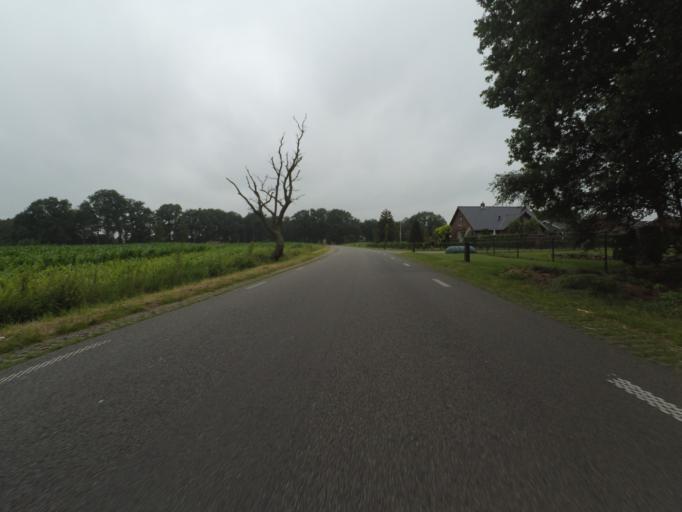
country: NL
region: Gelderland
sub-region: Gemeente Barneveld
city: Kootwijkerbroek
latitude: 52.1613
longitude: 5.6342
